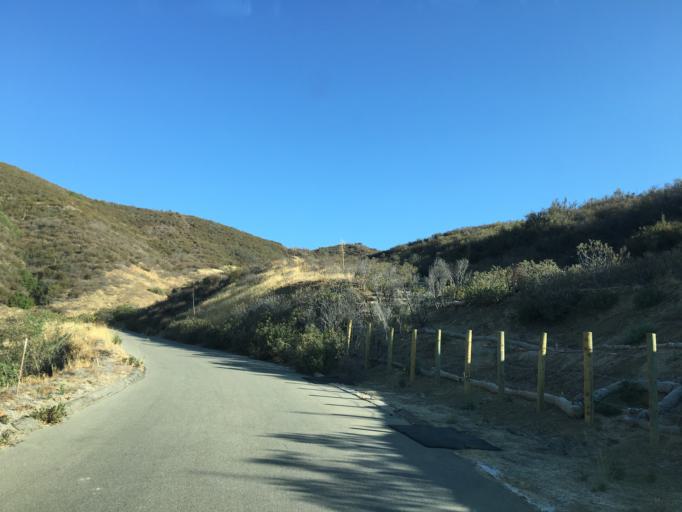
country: US
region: California
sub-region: Los Angeles County
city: Castaic
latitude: 34.5884
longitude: -118.6823
